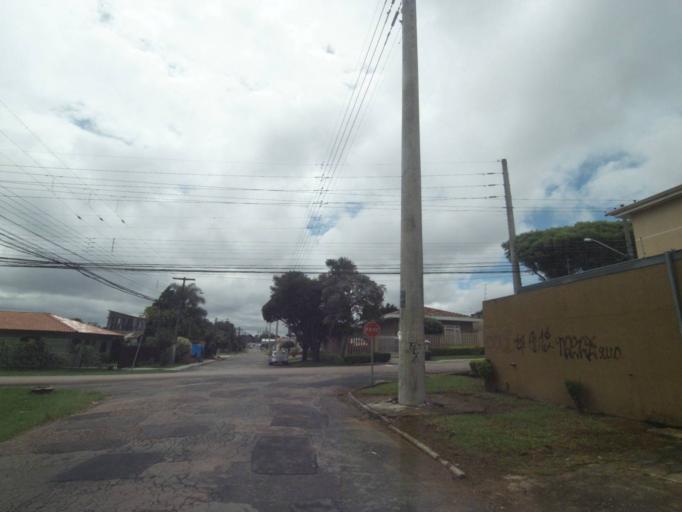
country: BR
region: Parana
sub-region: Curitiba
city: Curitiba
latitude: -25.4874
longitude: -49.3114
